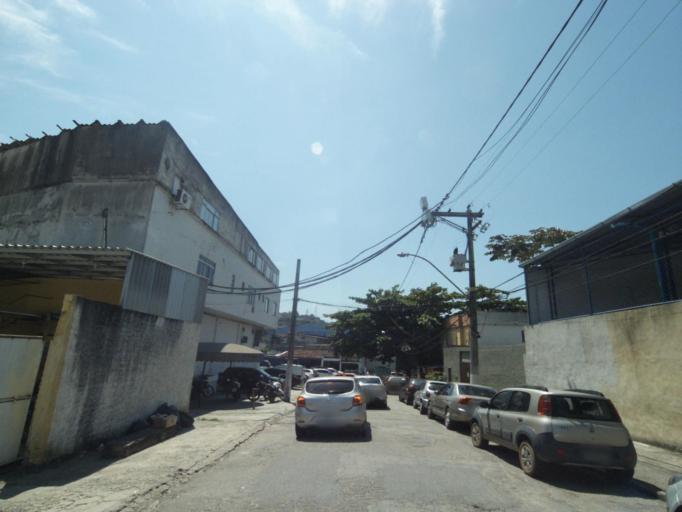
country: BR
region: Rio de Janeiro
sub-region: Niteroi
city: Niteroi
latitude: -22.9087
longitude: -43.0667
